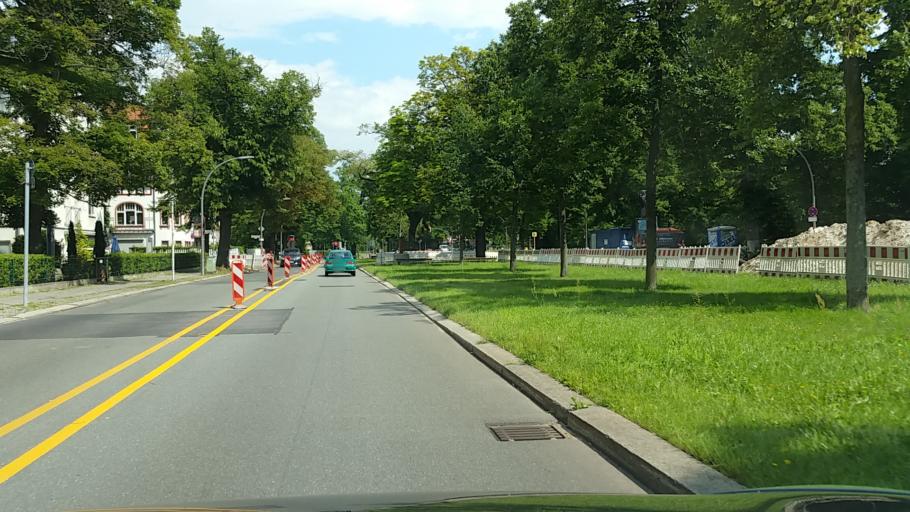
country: DE
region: Berlin
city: Spandau
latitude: 52.5553
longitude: 13.1961
